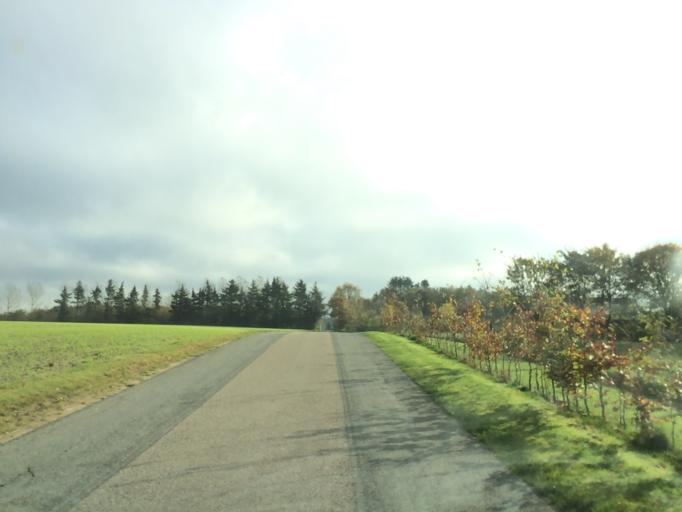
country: DK
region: Central Jutland
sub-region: Holstebro Kommune
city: Holstebro
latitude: 56.3503
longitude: 8.5644
